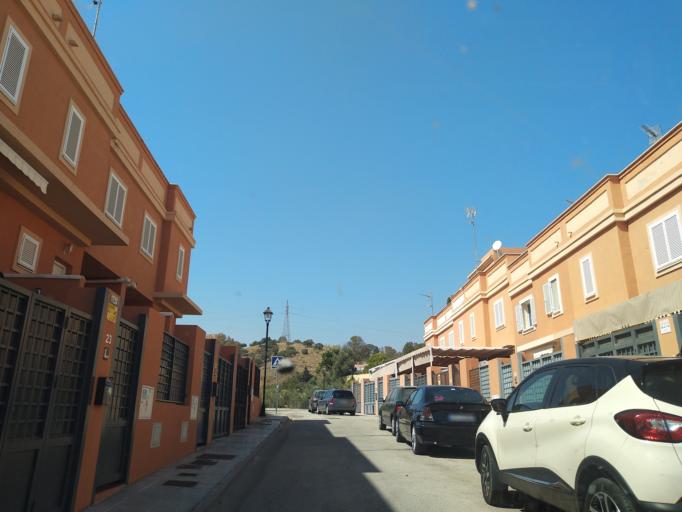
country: ES
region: Andalusia
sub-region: Provincia de Malaga
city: Valdes
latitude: 36.7208
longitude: -4.1994
